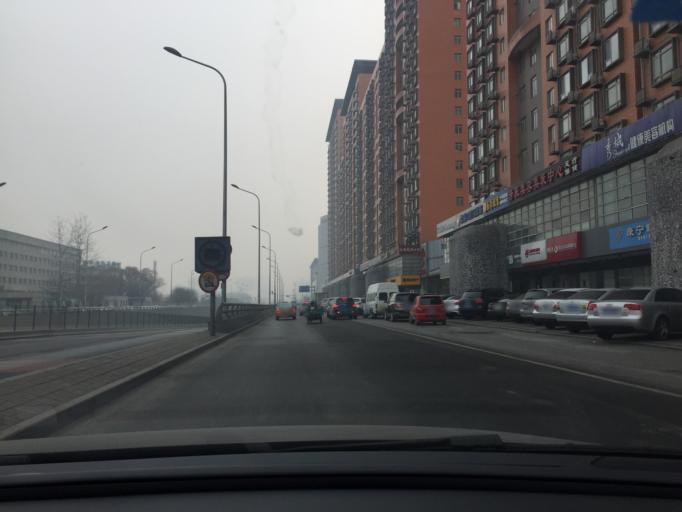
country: CN
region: Beijing
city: Datun
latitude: 40.0004
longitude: 116.3766
